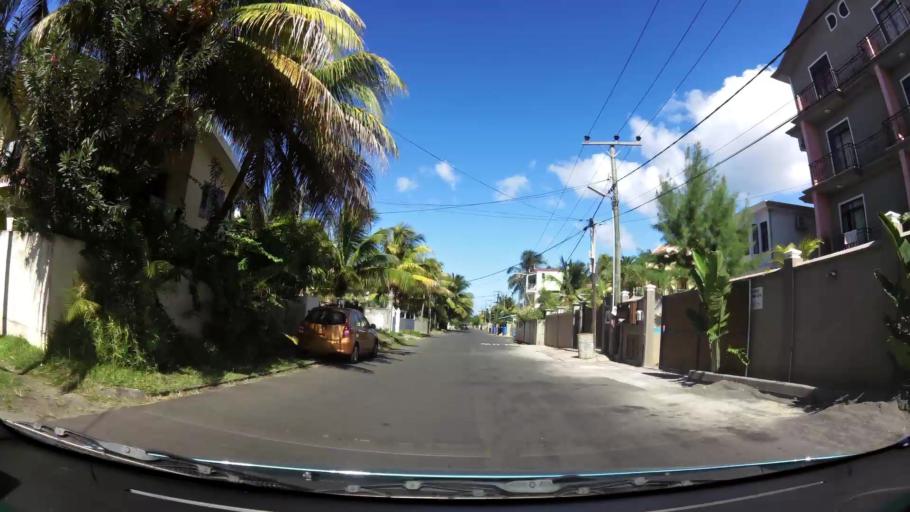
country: MU
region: Black River
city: Flic en Flac
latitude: -20.2867
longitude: 57.3672
